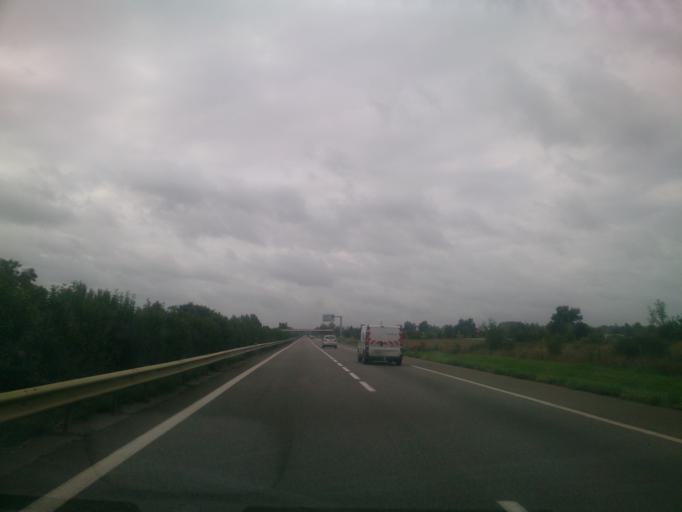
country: FR
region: Midi-Pyrenees
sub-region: Departement de la Haute-Garonne
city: Le Fauga
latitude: 43.3883
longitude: 1.2844
